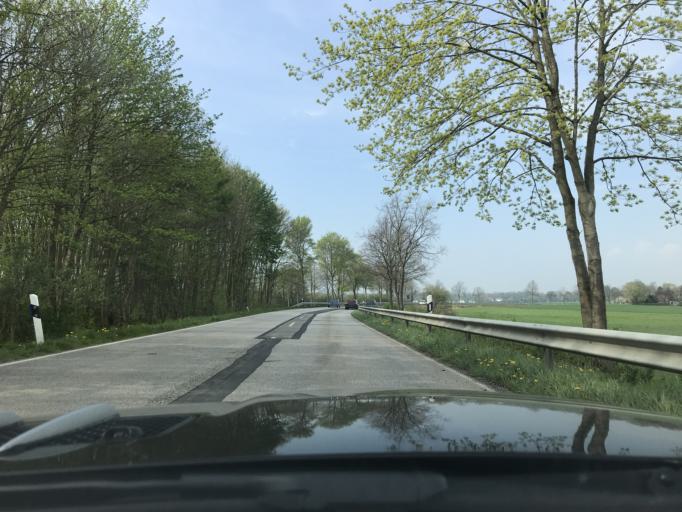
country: DE
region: Schleswig-Holstein
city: Riepsdorf
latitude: 54.1951
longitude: 11.0066
